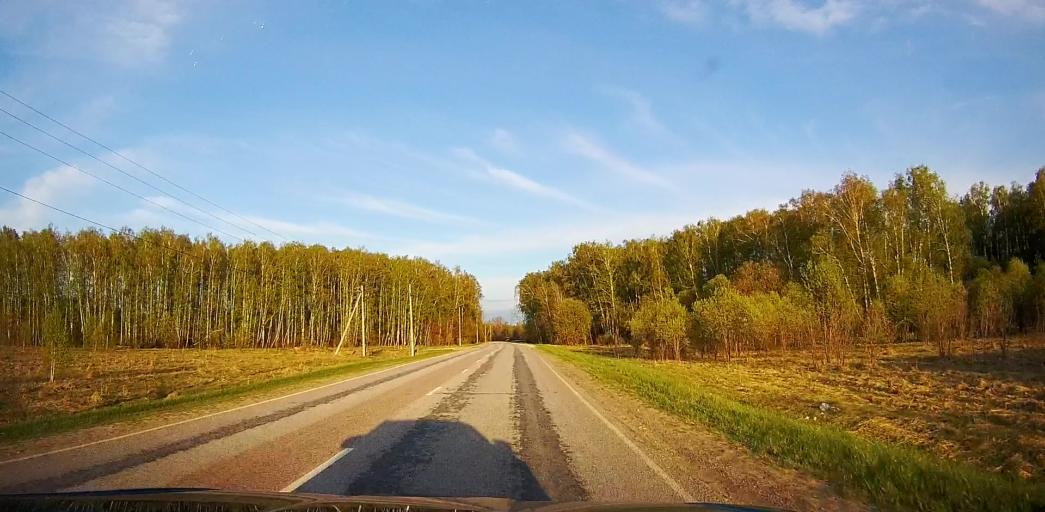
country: RU
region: Moskovskaya
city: Meshcherino
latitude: 55.2286
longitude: 38.3829
